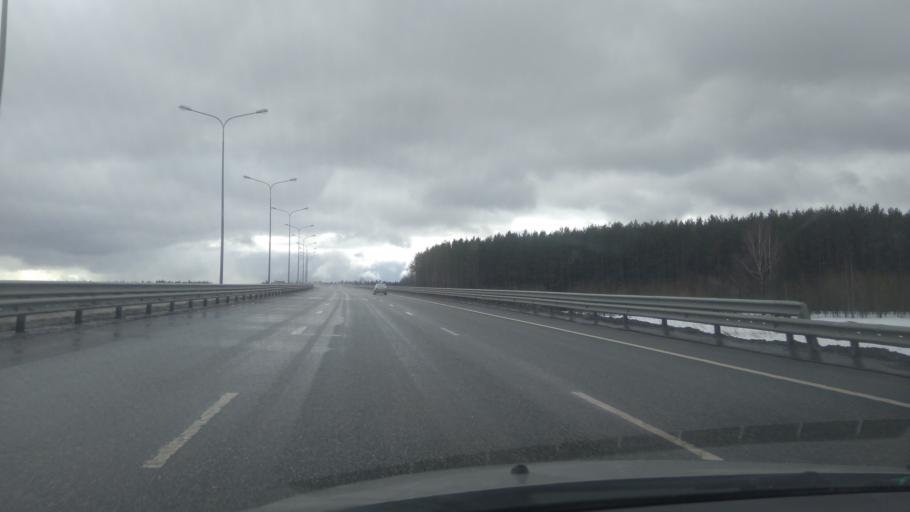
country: RU
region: Perm
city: Bershet'
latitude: 57.7125
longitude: 56.3624
